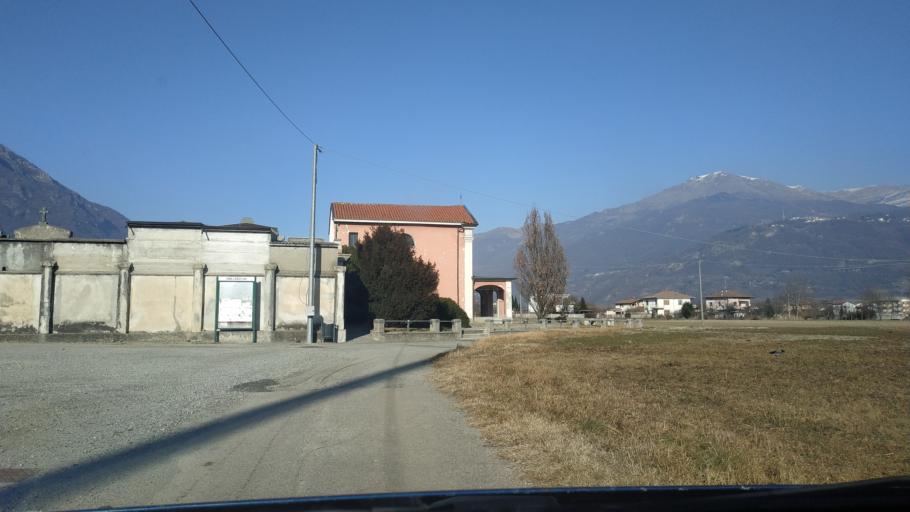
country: IT
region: Piedmont
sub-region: Provincia di Torino
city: Montalto Dora
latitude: 45.4904
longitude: 7.8554
